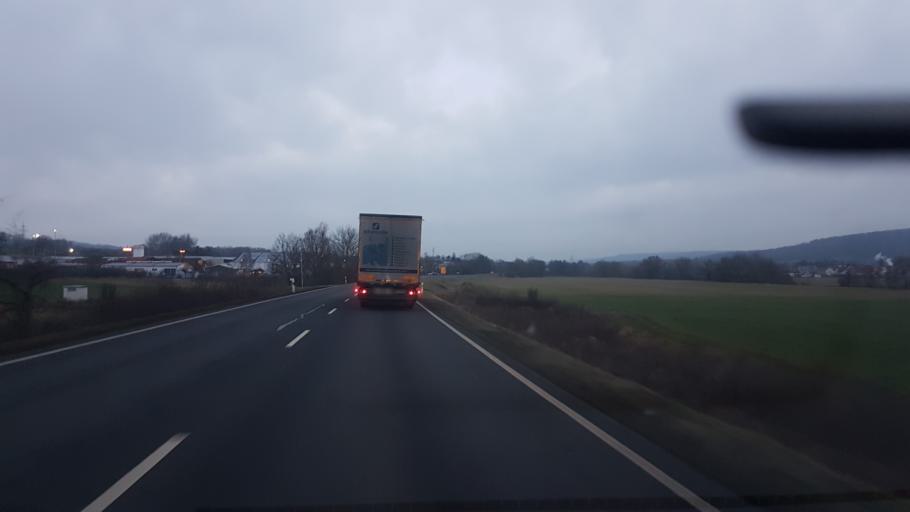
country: DE
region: Bavaria
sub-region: Regierungsbezirk Unterfranken
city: Rentweinsdorf
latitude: 50.0862
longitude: 10.7902
